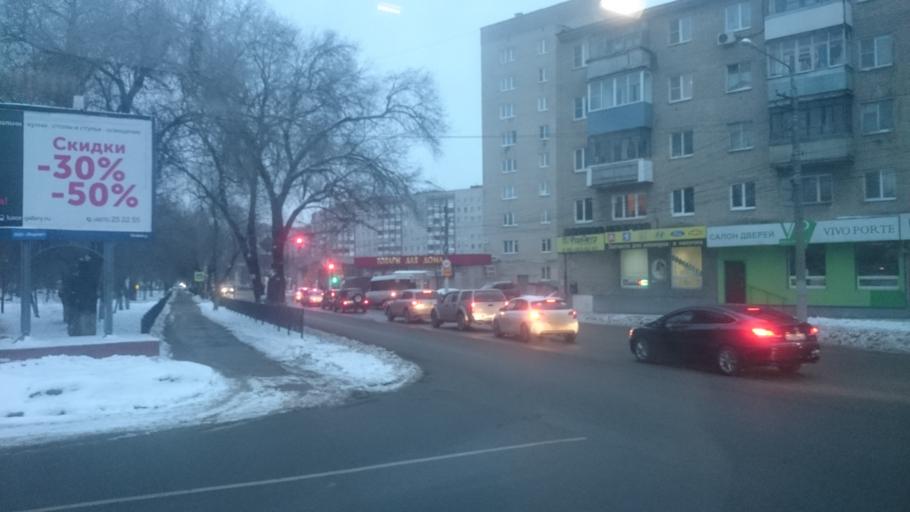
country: RU
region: Tula
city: Tula
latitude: 54.1763
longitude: 37.6307
